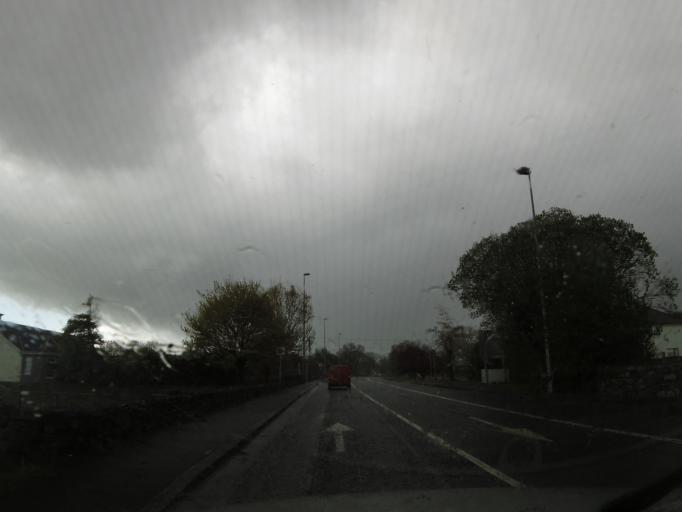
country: IE
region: Connaught
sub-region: County Galway
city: Claregalway
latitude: 53.3364
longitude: -8.9519
